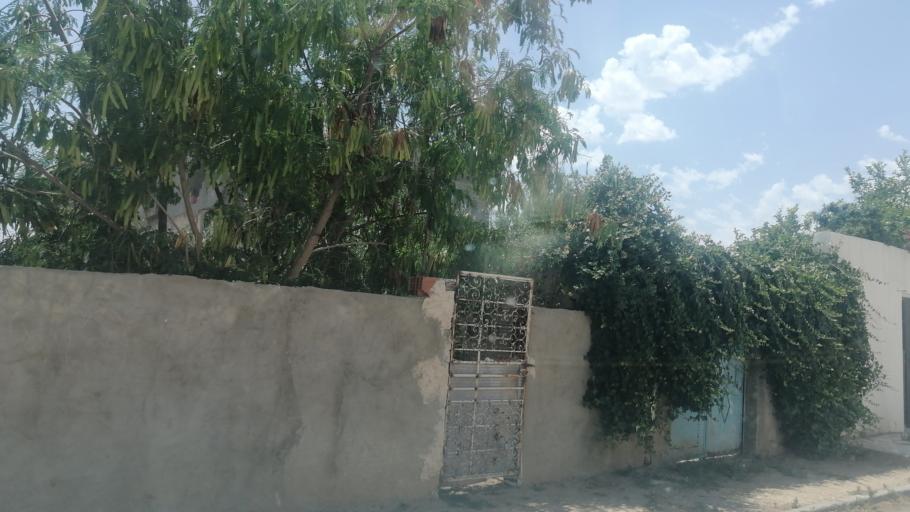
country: TN
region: Al Qayrawan
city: Sbikha
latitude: 36.1212
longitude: 10.0935
